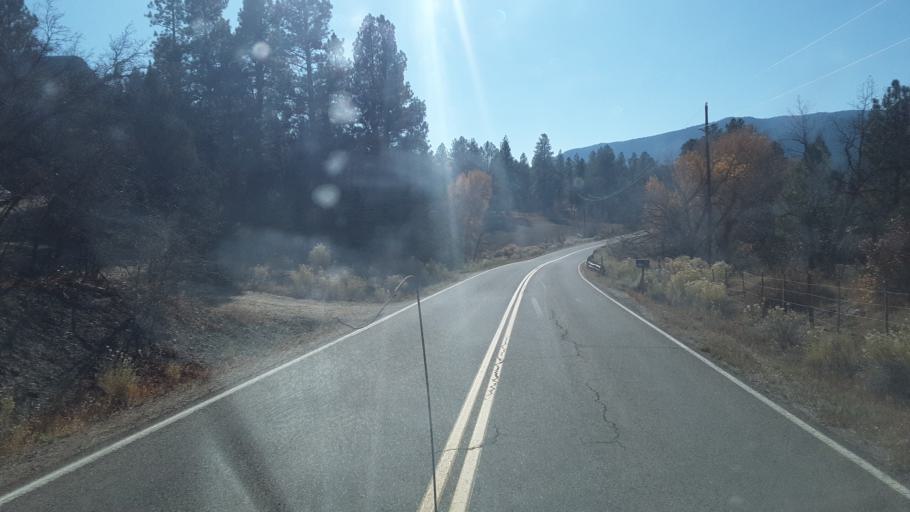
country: US
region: Colorado
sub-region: La Plata County
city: Durango
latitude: 37.4153
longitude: -107.8056
